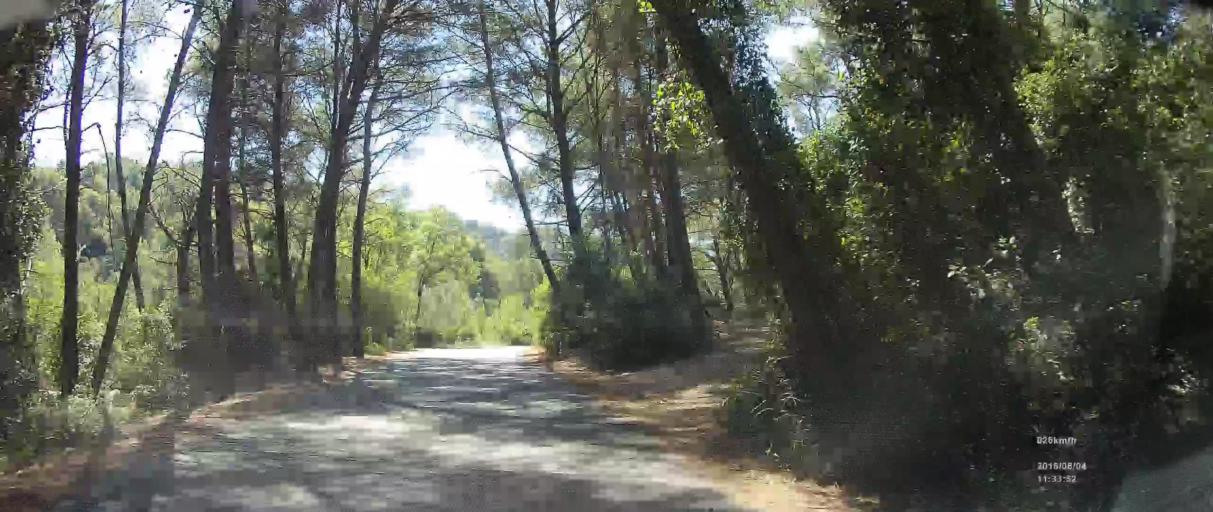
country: HR
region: Dubrovacko-Neretvanska
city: Blato
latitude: 42.7874
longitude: 17.3677
